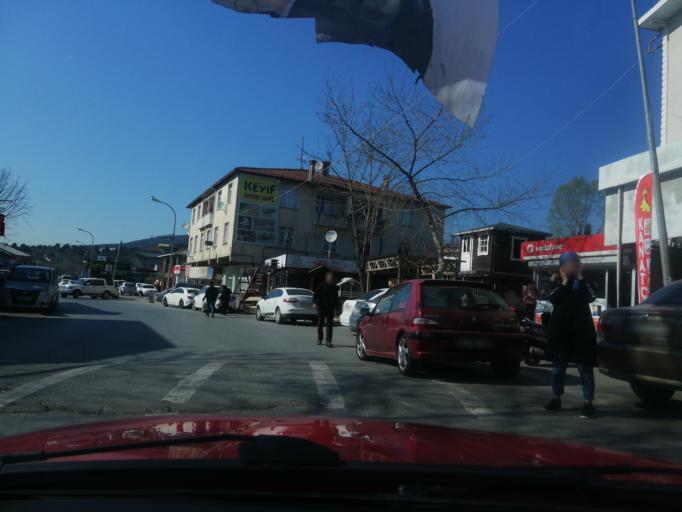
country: TR
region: Istanbul
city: Umraniye
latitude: 41.0826
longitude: 29.1386
